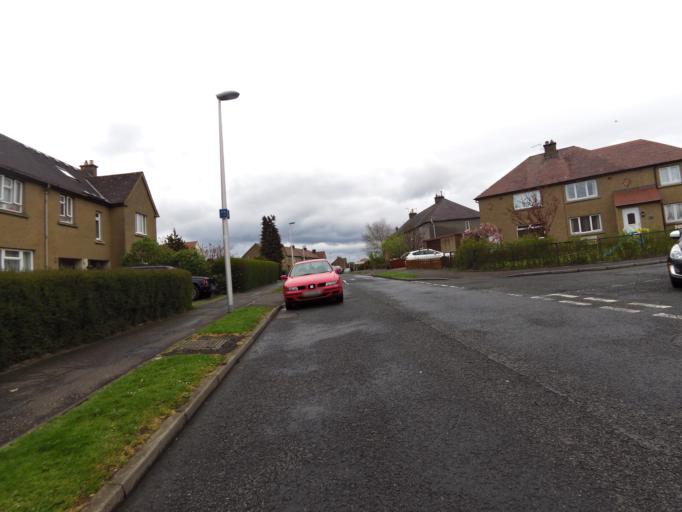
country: GB
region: Scotland
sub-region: Edinburgh
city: Queensferry
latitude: 55.9860
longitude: -3.3937
